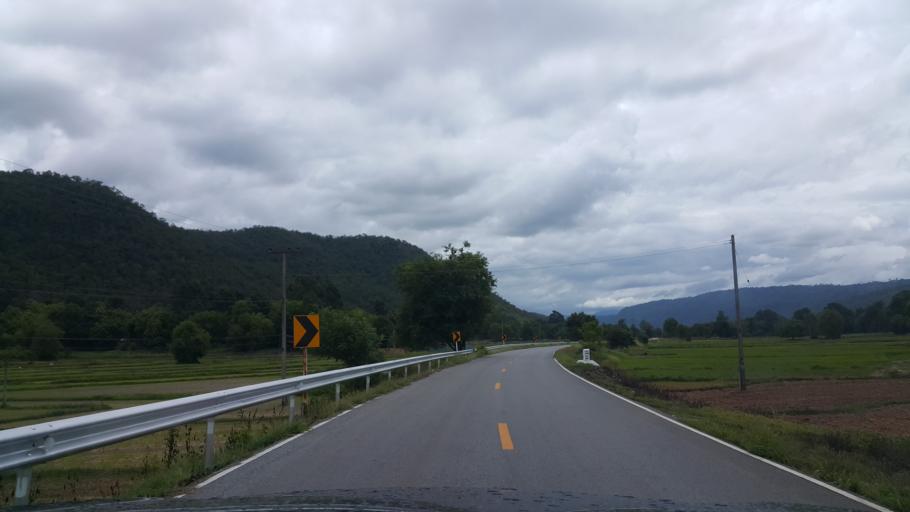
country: TH
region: Phitsanulok
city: Chat Trakan
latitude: 17.3147
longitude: 100.6746
